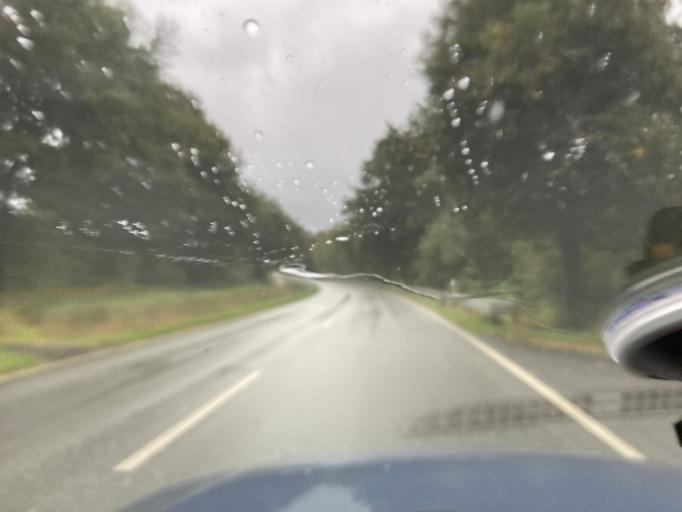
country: DE
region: Schleswig-Holstein
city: Nordhastedt
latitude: 54.1943
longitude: 9.1940
